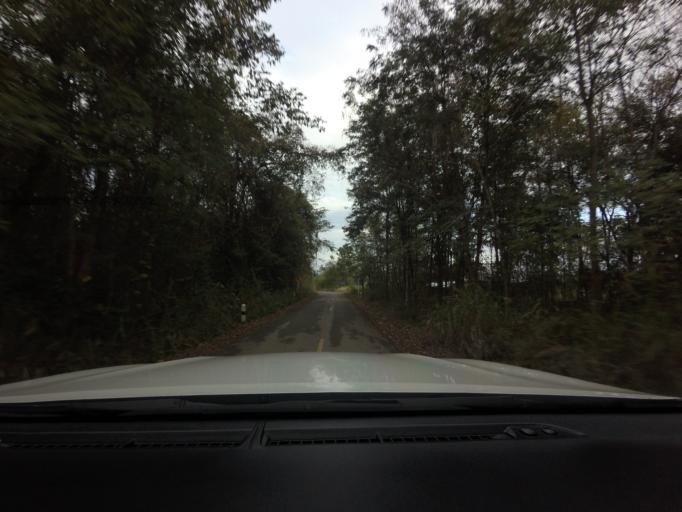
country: TH
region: Nakhon Ratchasima
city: Wang Nam Khiao
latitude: 14.4696
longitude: 101.6595
